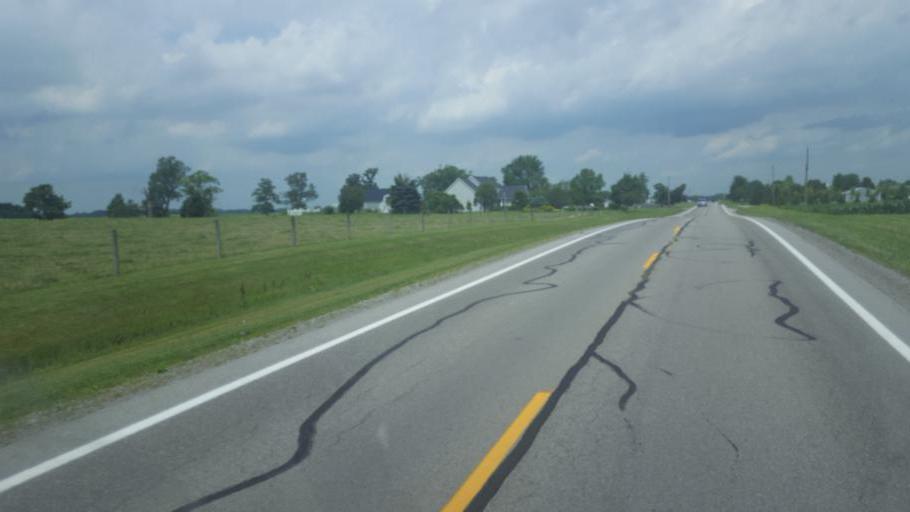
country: US
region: Ohio
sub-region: Hardin County
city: Kenton
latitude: 40.6033
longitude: -83.5946
